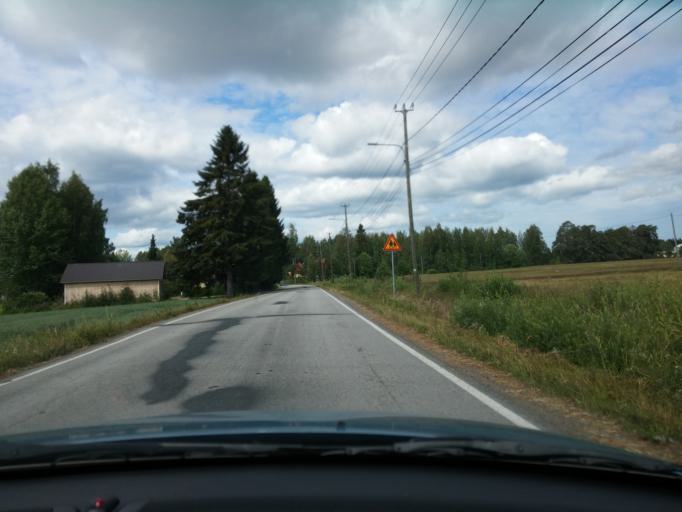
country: FI
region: Central Finland
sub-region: Saarijaervi-Viitasaari
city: Saarijaervi
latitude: 62.7346
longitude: 25.1859
